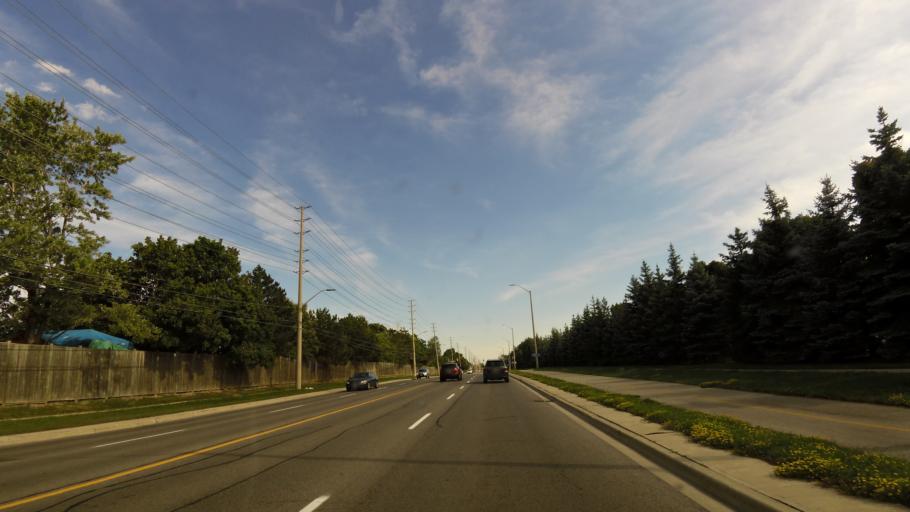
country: CA
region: Ontario
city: Mississauga
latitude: 43.5287
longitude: -79.6897
